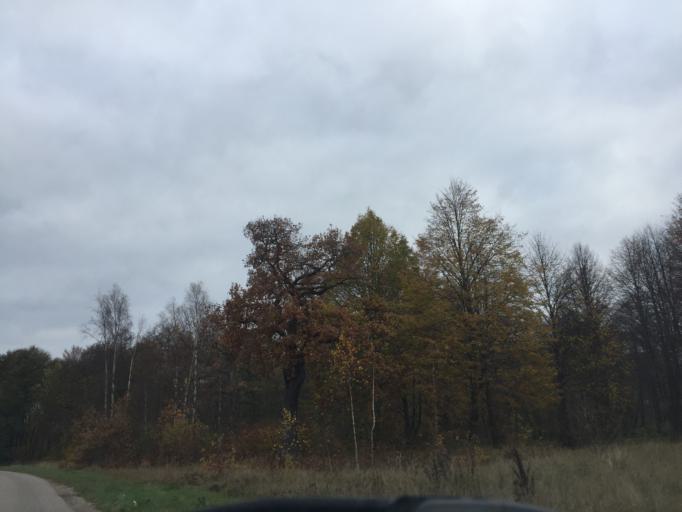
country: LV
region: Liepaja
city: Vec-Liepaja
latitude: 56.5472
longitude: 21.0786
